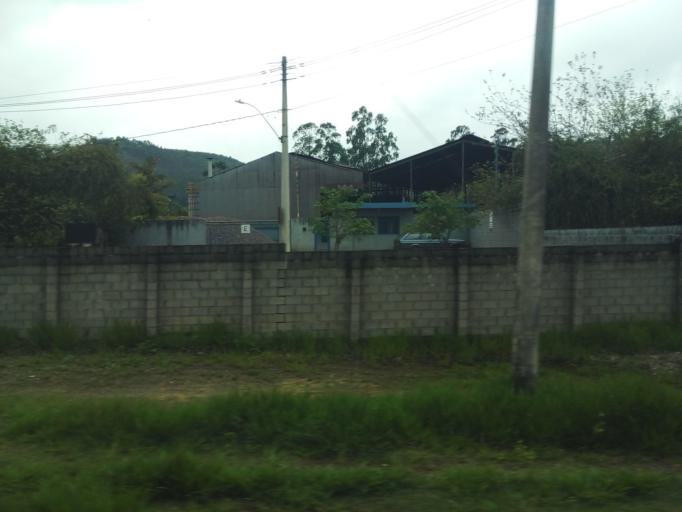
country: BR
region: Minas Gerais
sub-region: Rio Piracicaba
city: Rio Piracicaba
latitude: -19.9509
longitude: -43.1830
